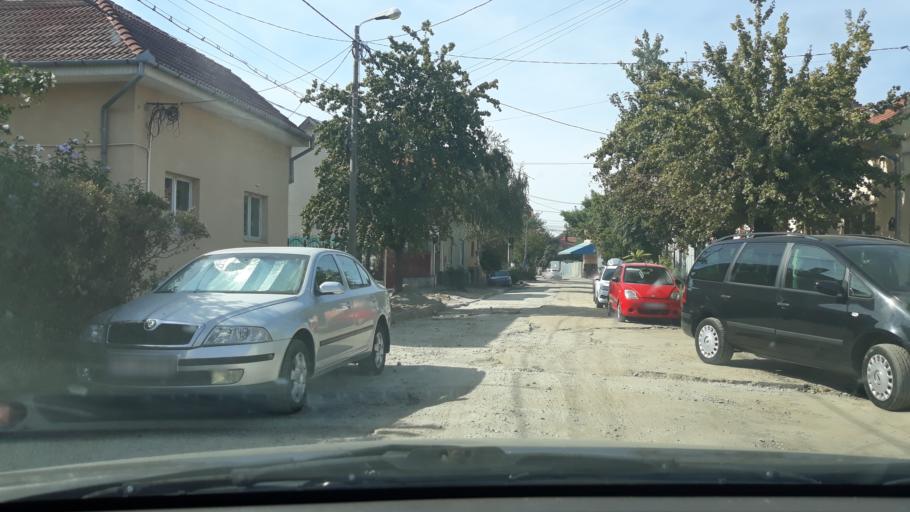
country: RO
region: Bihor
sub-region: Comuna Biharea
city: Oradea
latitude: 47.0469
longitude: 21.9388
